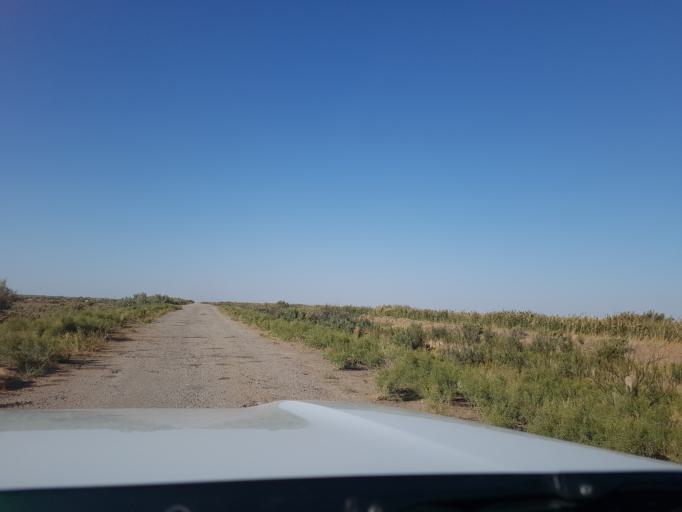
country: IR
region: Razavi Khorasan
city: Sarakhs
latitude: 36.9510
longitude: 61.3800
